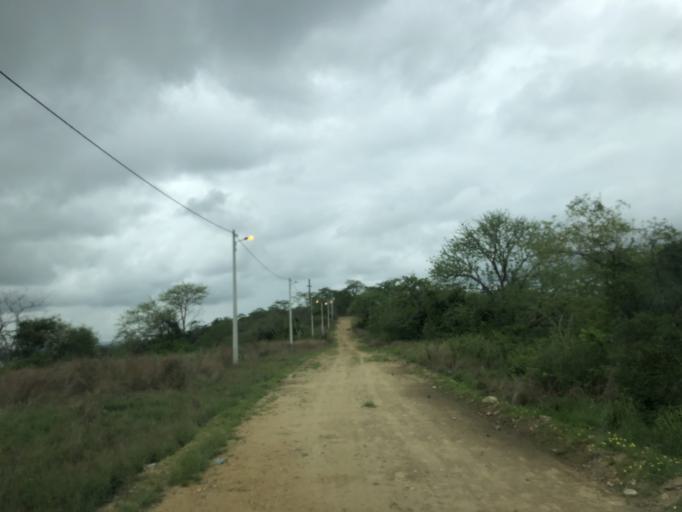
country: AO
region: Cuanza Norte
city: N'dalatando
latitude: -9.6283
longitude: 14.2539
